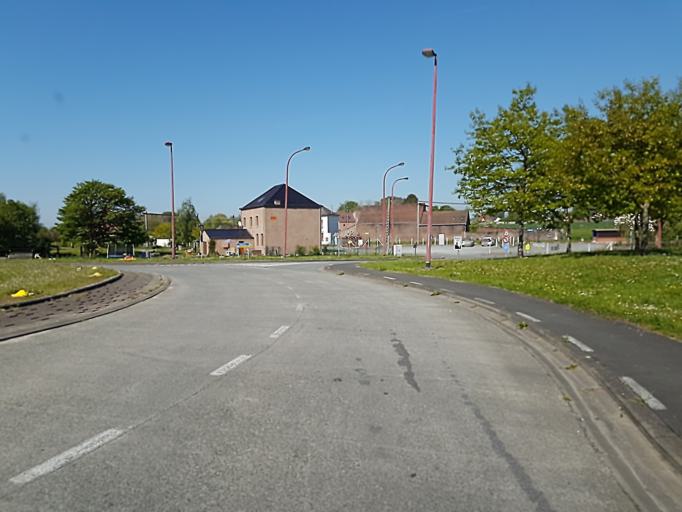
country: BE
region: Wallonia
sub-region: Province du Hainaut
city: Ath
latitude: 50.6608
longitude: 3.7950
